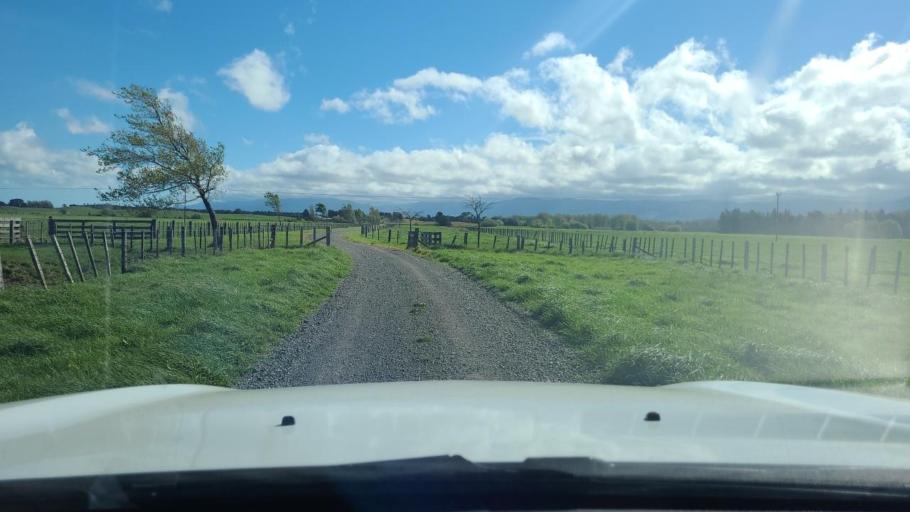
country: NZ
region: Wellington
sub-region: South Wairarapa District
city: Waipawa
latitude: -41.1881
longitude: 175.3574
